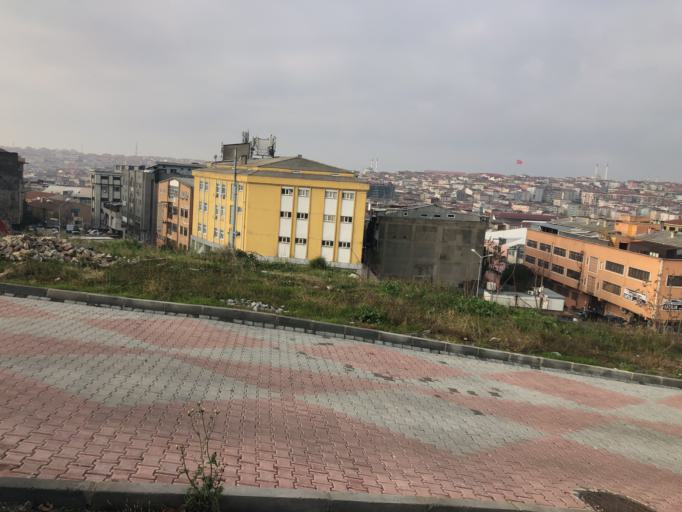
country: TR
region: Istanbul
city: merter keresteciler
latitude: 41.0229
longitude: 28.8861
